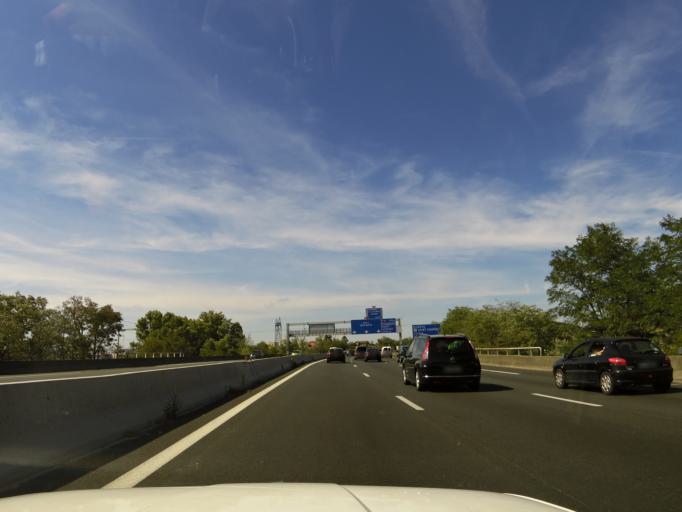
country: FR
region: Rhone-Alpes
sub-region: Departement de l'Isere
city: Chasse-sur-Rhone
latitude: 45.5759
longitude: 4.8053
